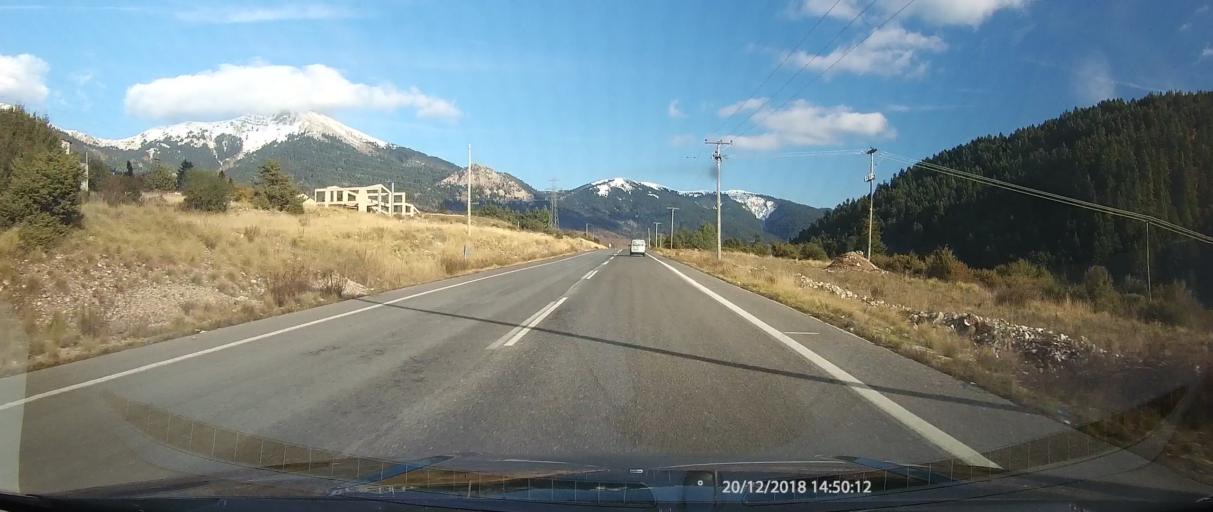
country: GR
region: Central Greece
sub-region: Nomos Evrytanias
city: Karpenisi
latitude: 38.9055
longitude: 21.8202
